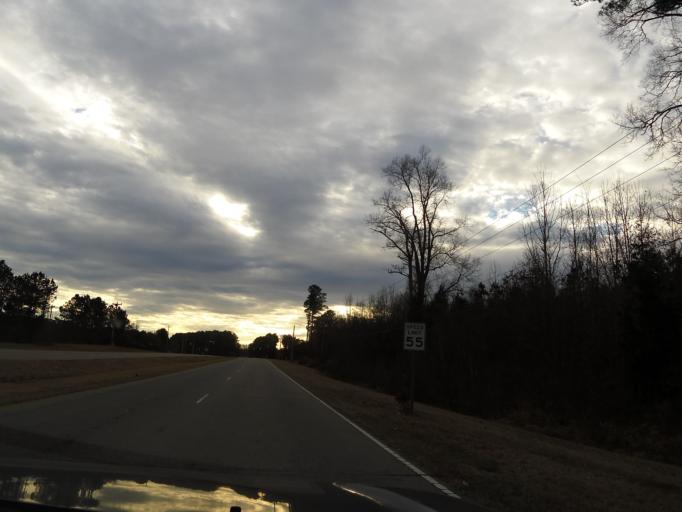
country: US
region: North Carolina
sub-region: Nash County
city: Rocky Mount
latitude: 36.0450
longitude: -77.7575
